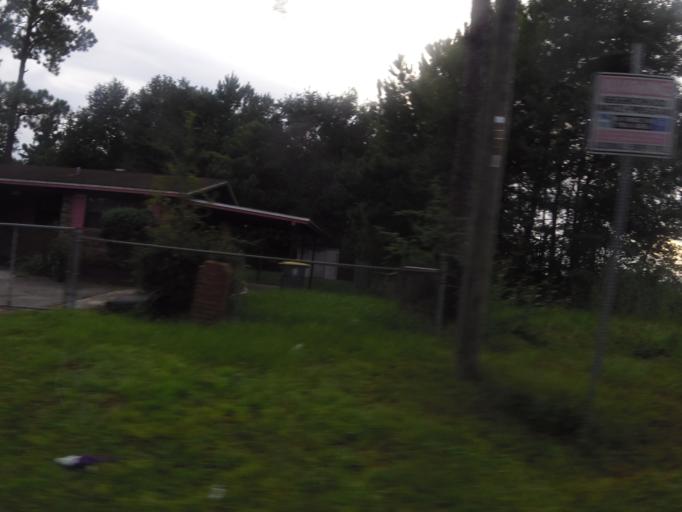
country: US
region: Florida
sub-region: Duval County
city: Jacksonville
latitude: 30.3621
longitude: -81.7085
